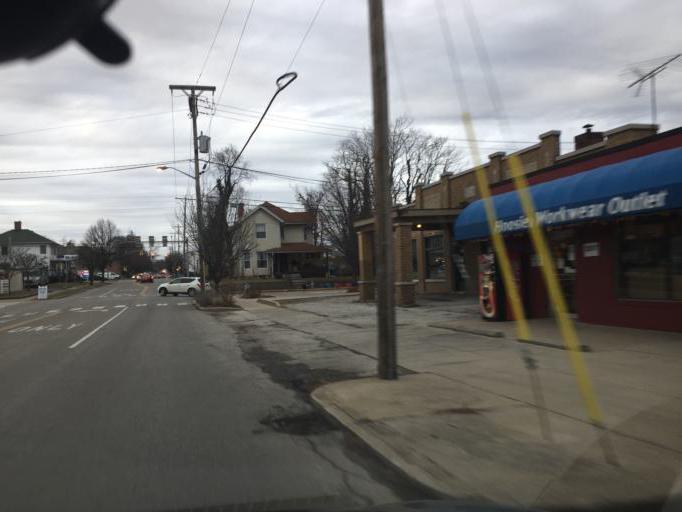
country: US
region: Indiana
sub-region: Monroe County
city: Bloomington
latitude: 39.1651
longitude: -86.5387
